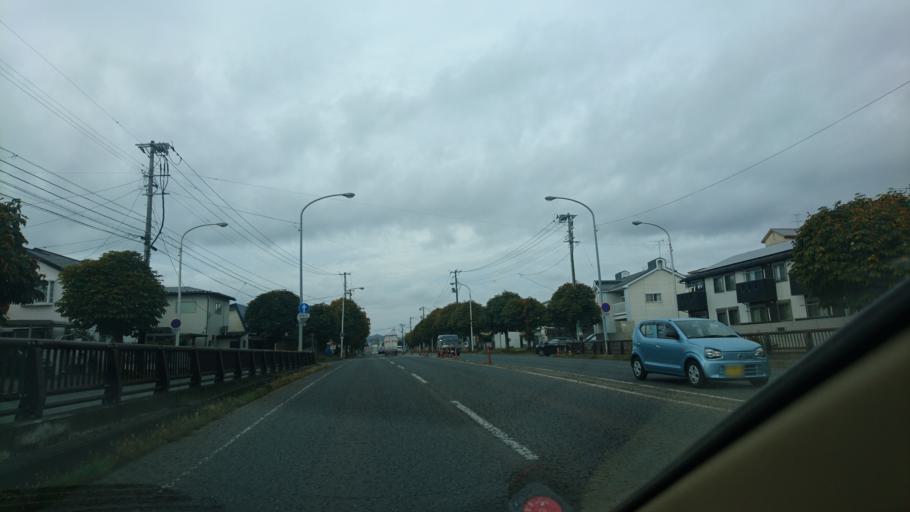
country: JP
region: Iwate
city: Morioka-shi
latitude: 39.6845
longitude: 141.1467
